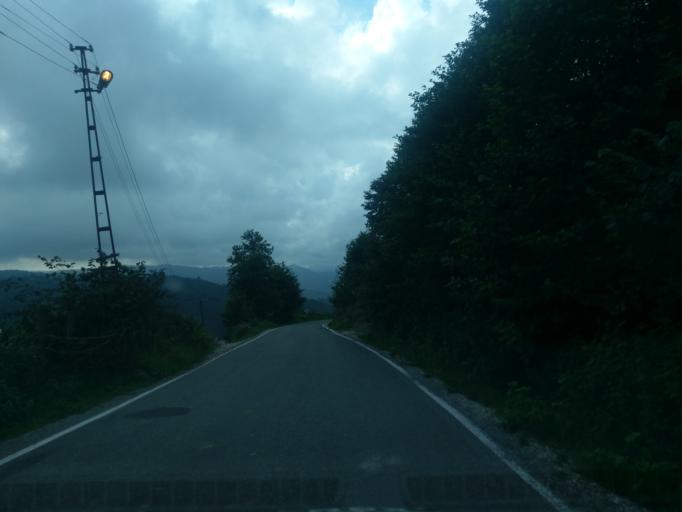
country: TR
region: Ordu
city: Gurgentepe
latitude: 40.8647
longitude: 37.6417
